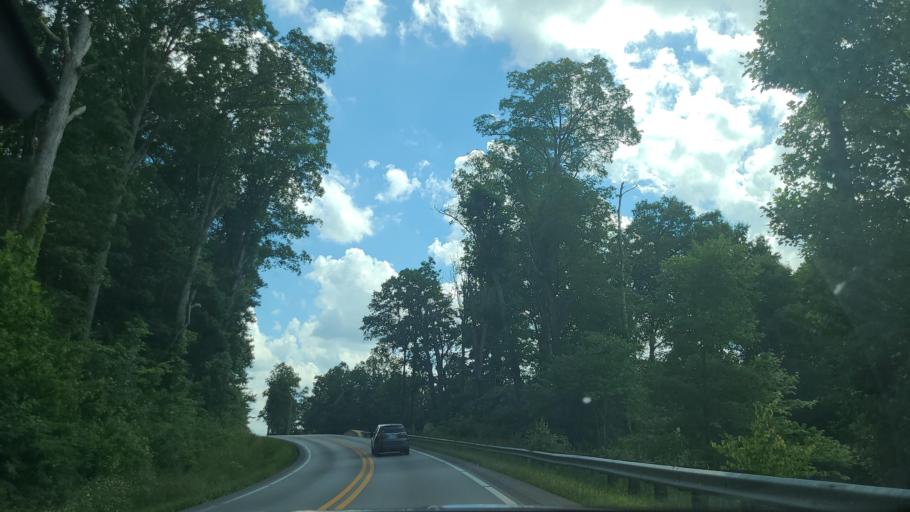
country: US
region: Kentucky
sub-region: Whitley County
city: Corbin
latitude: 36.8978
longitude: -84.1813
